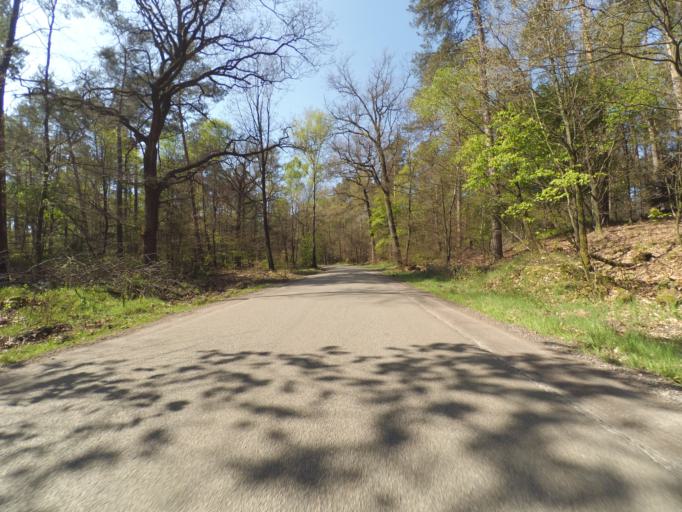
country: NL
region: Gelderland
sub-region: Gemeente Apeldoorn
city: Uddel
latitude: 52.3107
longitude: 5.7397
